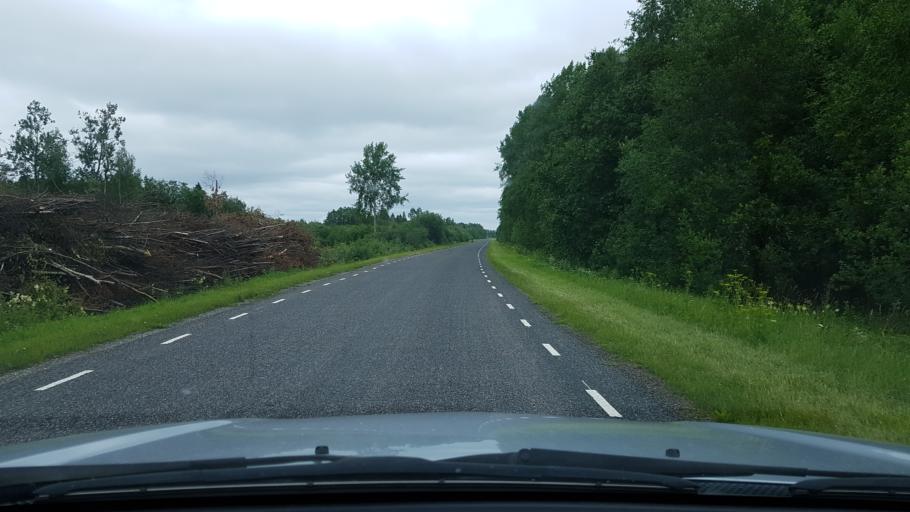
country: EE
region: Ida-Virumaa
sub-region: Narva-Joesuu linn
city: Narva-Joesuu
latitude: 59.3753
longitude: 28.0701
